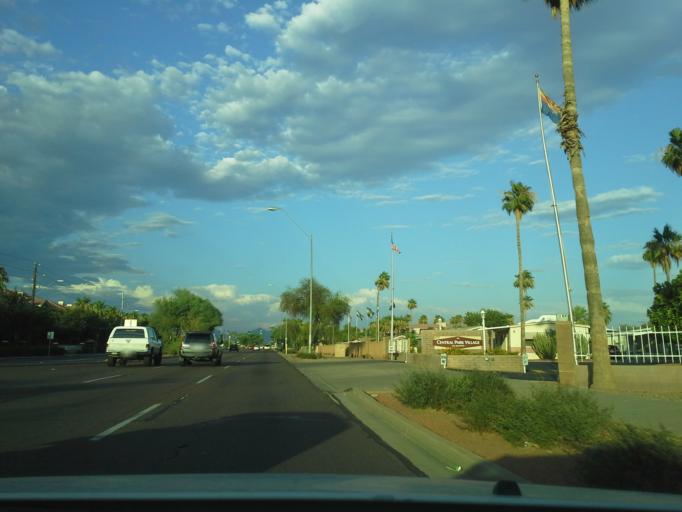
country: US
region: Arizona
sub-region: Maricopa County
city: Glendale
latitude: 33.6401
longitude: -112.0767
